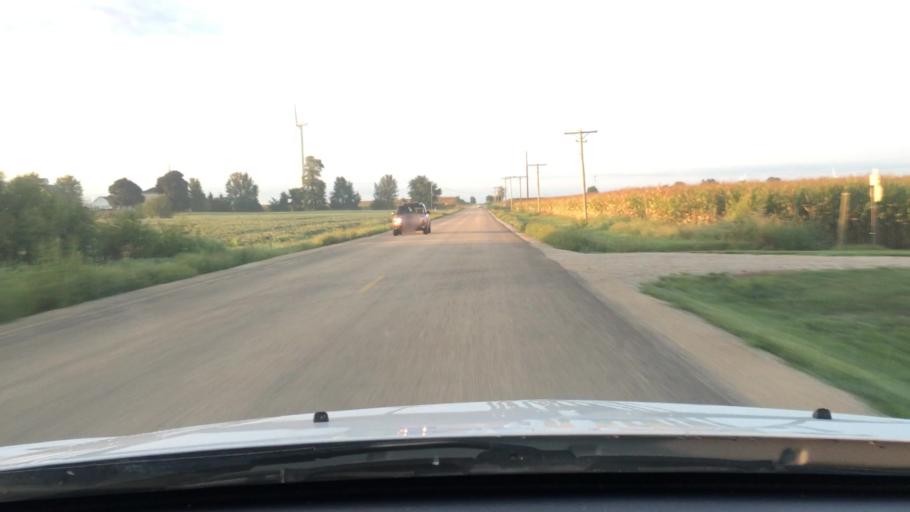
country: US
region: Illinois
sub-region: DeKalb County
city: Waterman
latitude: 41.8311
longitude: -88.7734
